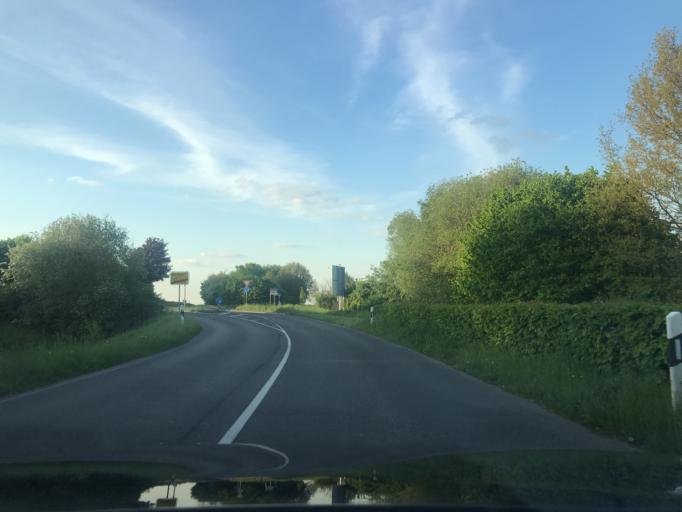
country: DE
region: North Rhine-Westphalia
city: Erkelenz
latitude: 51.0924
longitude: 6.3203
